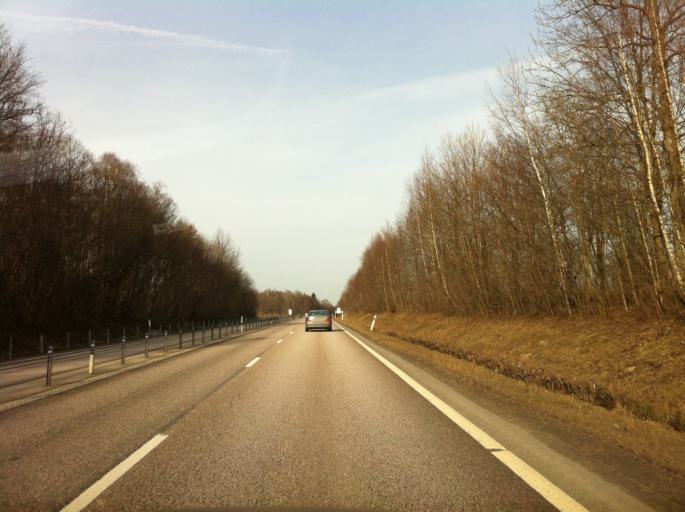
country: SE
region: Vaestra Goetaland
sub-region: Skovde Kommun
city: Stopen
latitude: 58.4570
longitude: 13.8479
